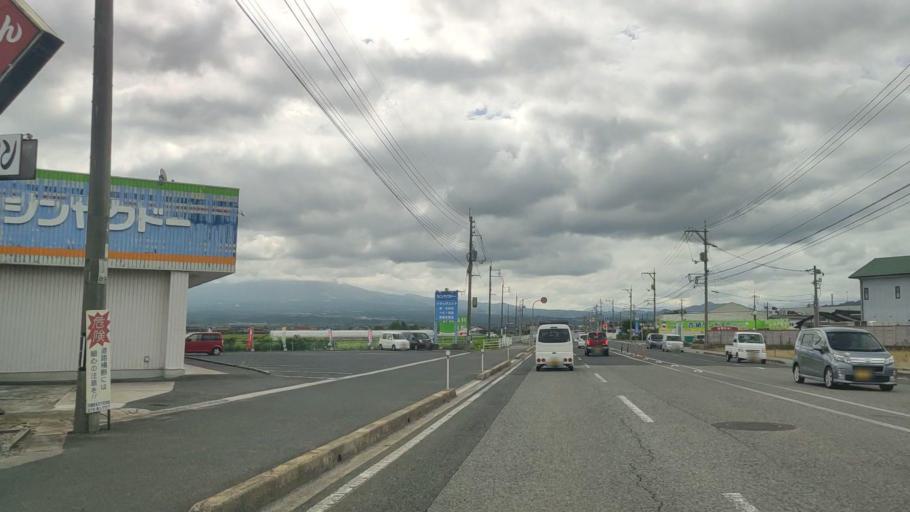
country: JP
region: Tottori
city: Yonago
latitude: 35.4011
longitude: 133.3734
